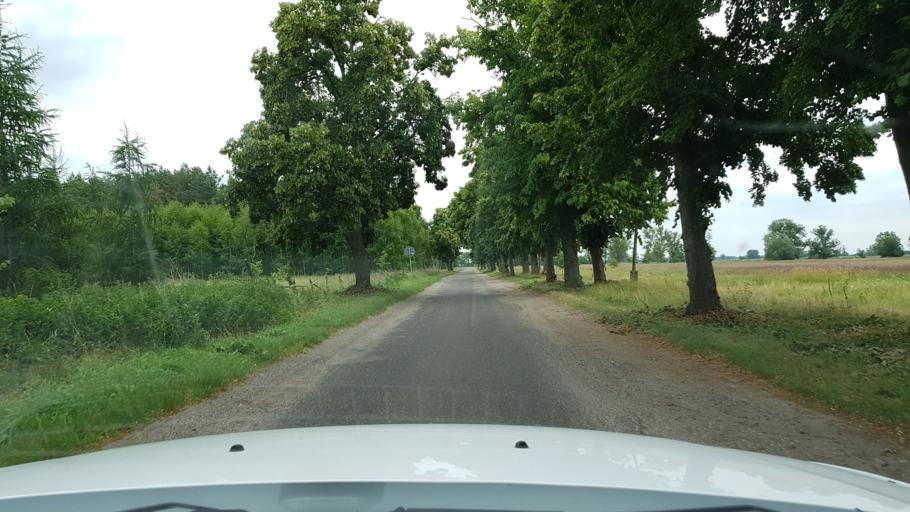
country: DE
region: Brandenburg
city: Manschnow
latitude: 52.6318
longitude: 14.5644
